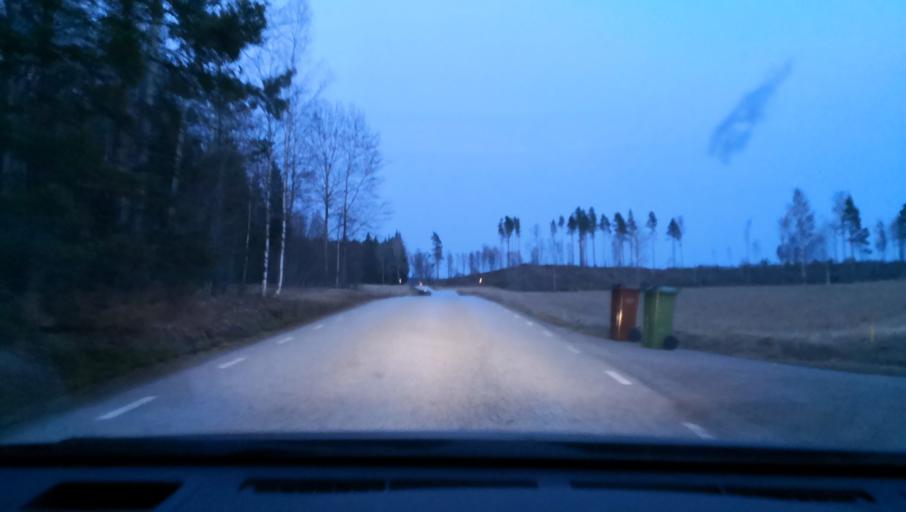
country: SE
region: OErebro
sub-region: Lindesbergs Kommun
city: Frovi
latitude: 59.5818
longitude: 15.4636
